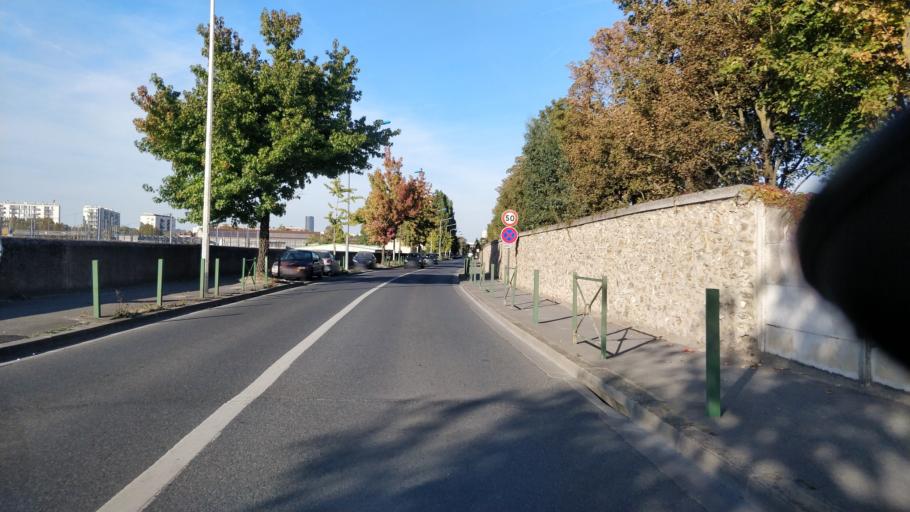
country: FR
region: Ile-de-France
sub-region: Departement des Hauts-de-Seine
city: Chatillon
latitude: 48.8063
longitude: 2.3040
